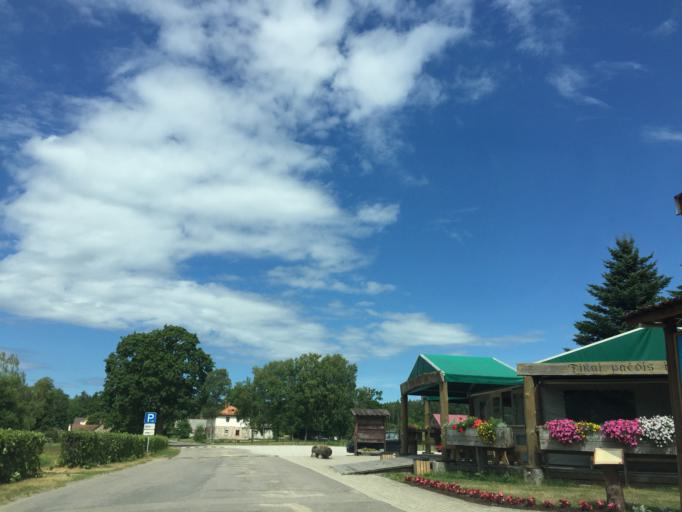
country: LV
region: Saulkrastu
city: Saulkrasti
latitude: 57.4051
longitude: 24.4246
